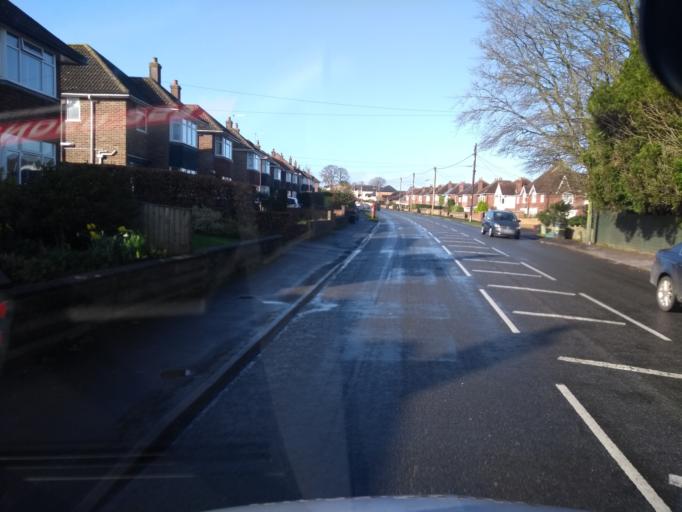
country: GB
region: England
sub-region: Somerset
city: Yeovil
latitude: 50.9581
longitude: -2.6263
